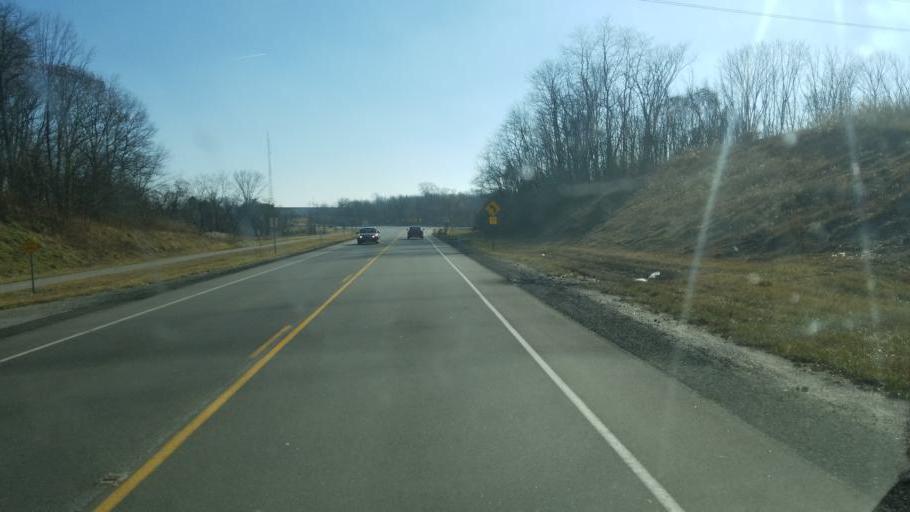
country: US
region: Ohio
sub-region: Geauga County
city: Chardon
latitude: 41.5953
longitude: -81.2292
